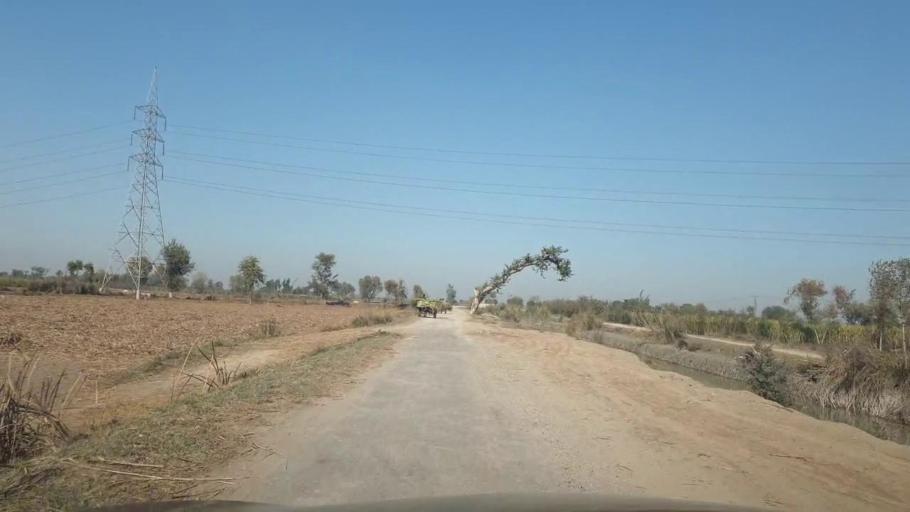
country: PK
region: Sindh
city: Ghotki
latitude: 27.9911
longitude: 69.4276
